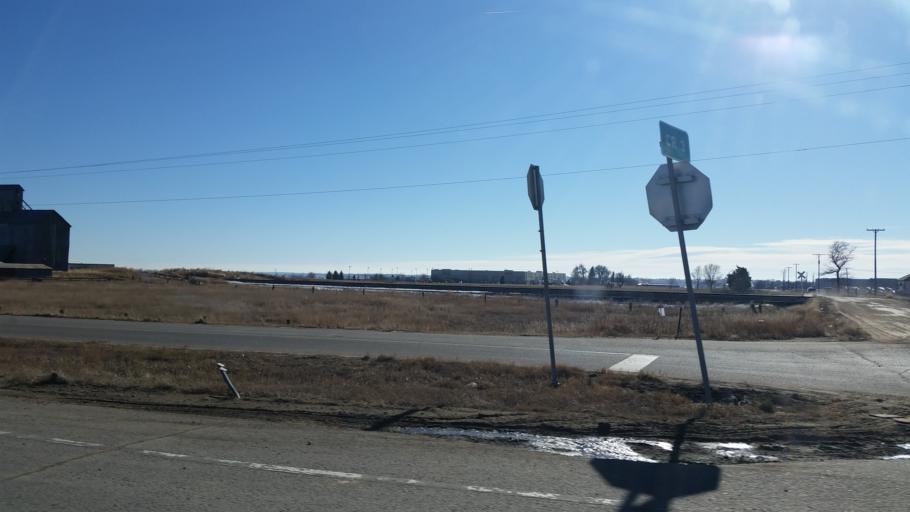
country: US
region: Colorado
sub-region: Weld County
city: Johnstown
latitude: 40.4074
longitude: -104.9643
